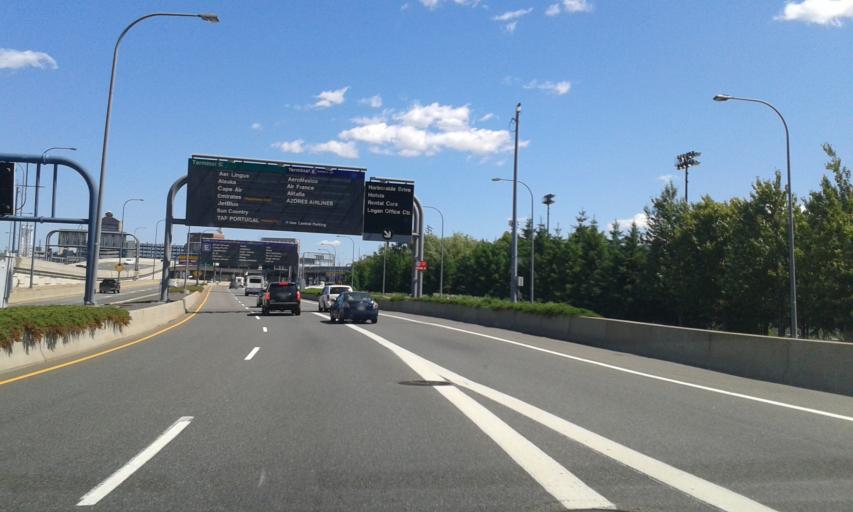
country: US
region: Massachusetts
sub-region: Suffolk County
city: Chelsea
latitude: 42.3726
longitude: -71.0292
